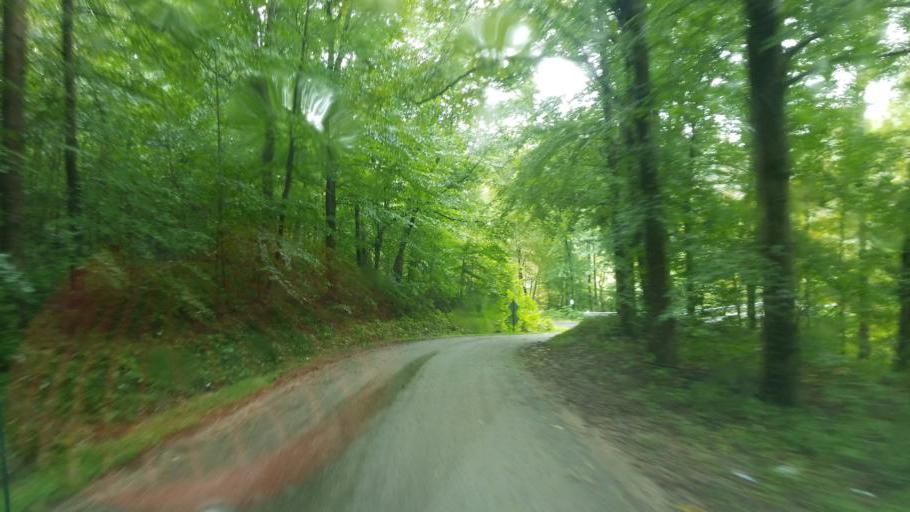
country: US
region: Ohio
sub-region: Adams County
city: Peebles
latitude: 38.8320
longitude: -83.2343
